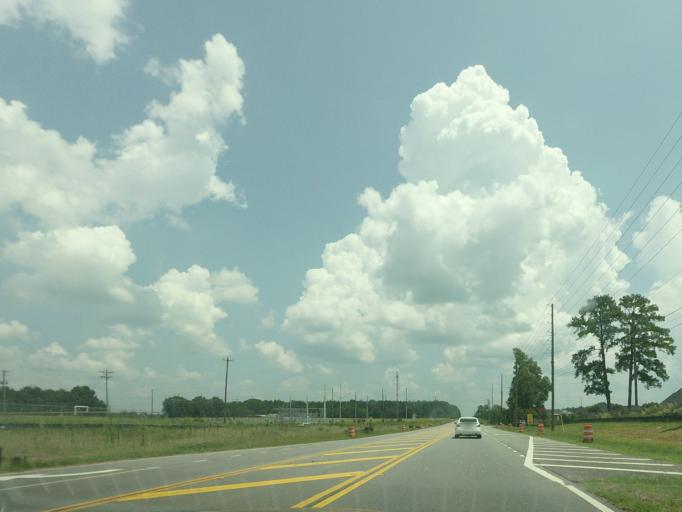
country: US
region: Georgia
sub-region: Houston County
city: Robins Air Force Base
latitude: 32.5437
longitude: -83.5859
